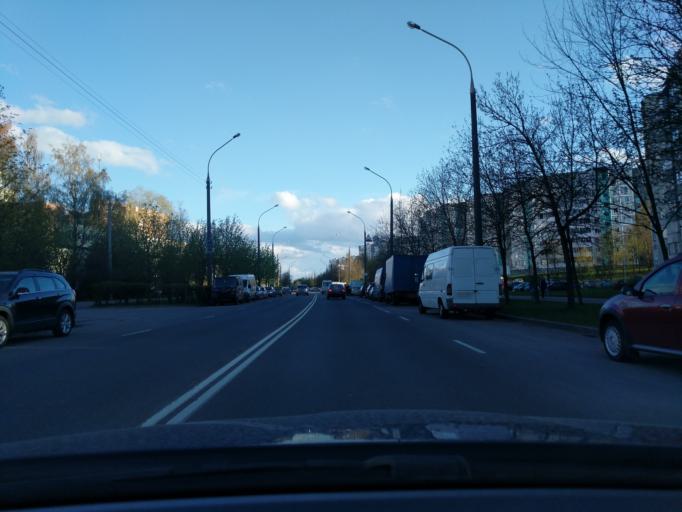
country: BY
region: Minsk
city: Novoye Medvezhino
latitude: 53.9135
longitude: 27.4502
